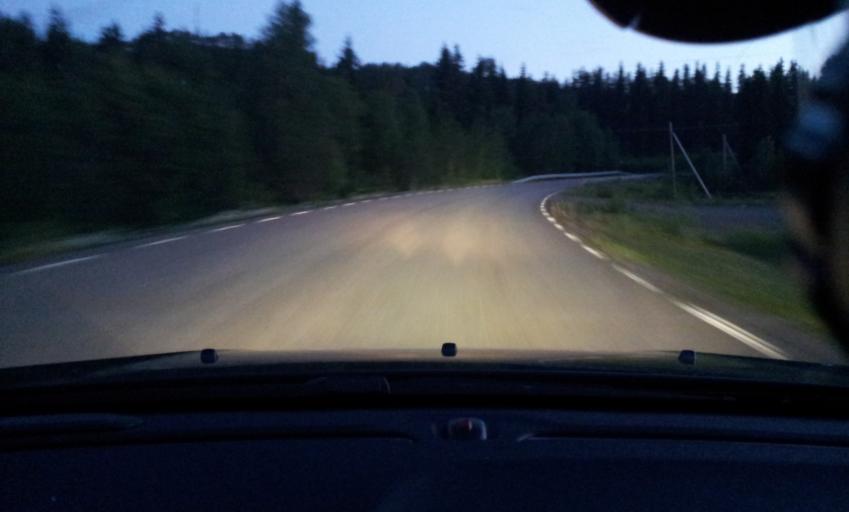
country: SE
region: Jaemtland
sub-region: Bergs Kommun
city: Hoverberg
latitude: 62.6588
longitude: 14.7434
